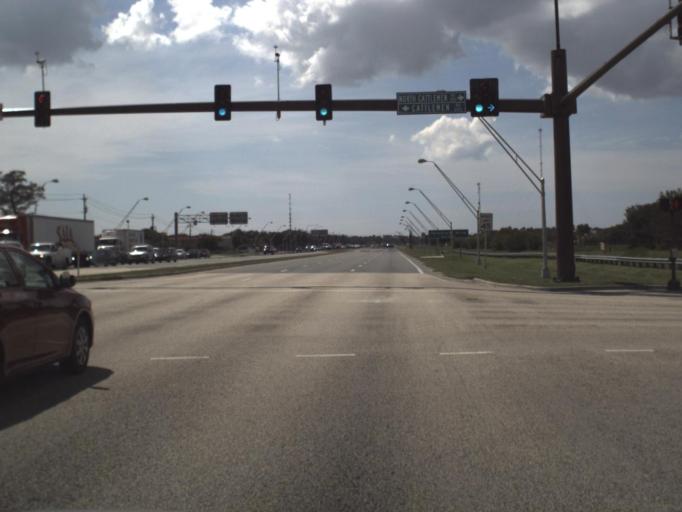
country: US
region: Florida
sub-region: Sarasota County
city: Fruitville
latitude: 27.3383
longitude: -82.4524
